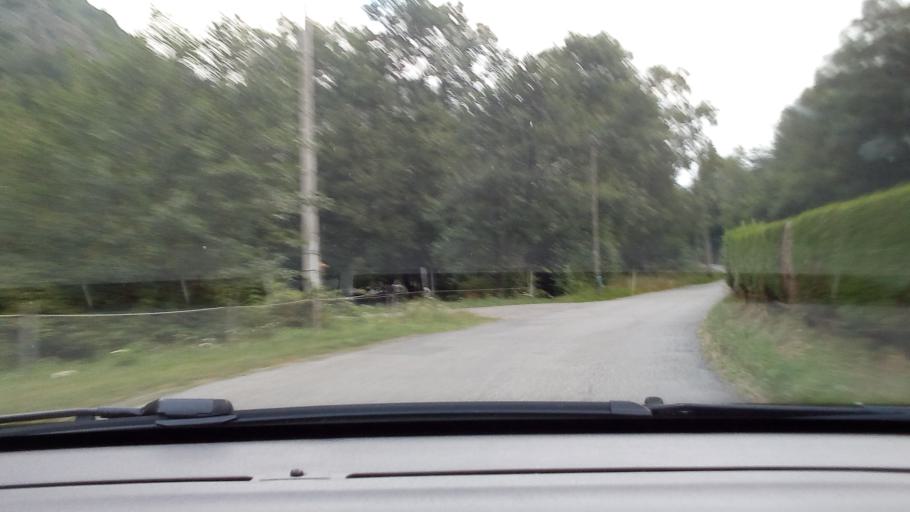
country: FR
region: Midi-Pyrenees
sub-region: Departement des Hautes-Pyrenees
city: Cauterets
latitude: 42.9295
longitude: -0.1805
